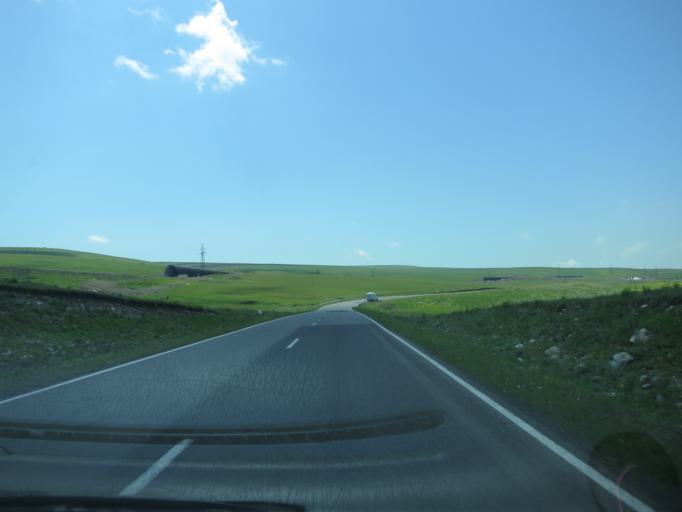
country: GE
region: Samtskhe-Javakheti
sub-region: Ninotsminda
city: Ninotsminda
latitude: 41.4184
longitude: 43.8333
